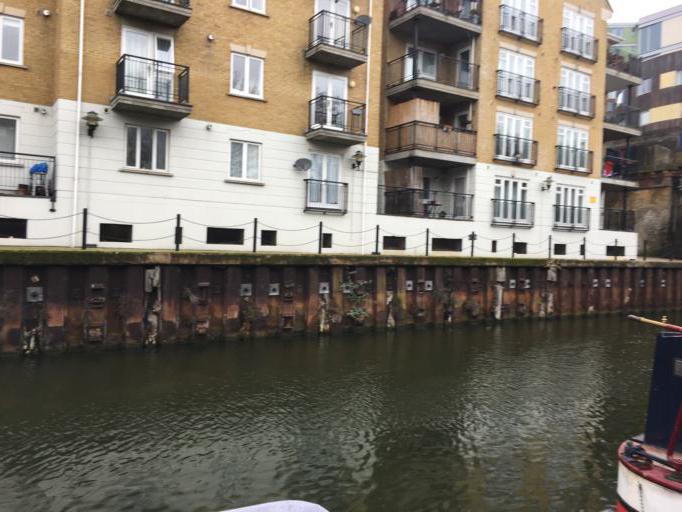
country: GB
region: England
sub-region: Greater London
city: Poplar
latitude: 51.5110
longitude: -0.0327
